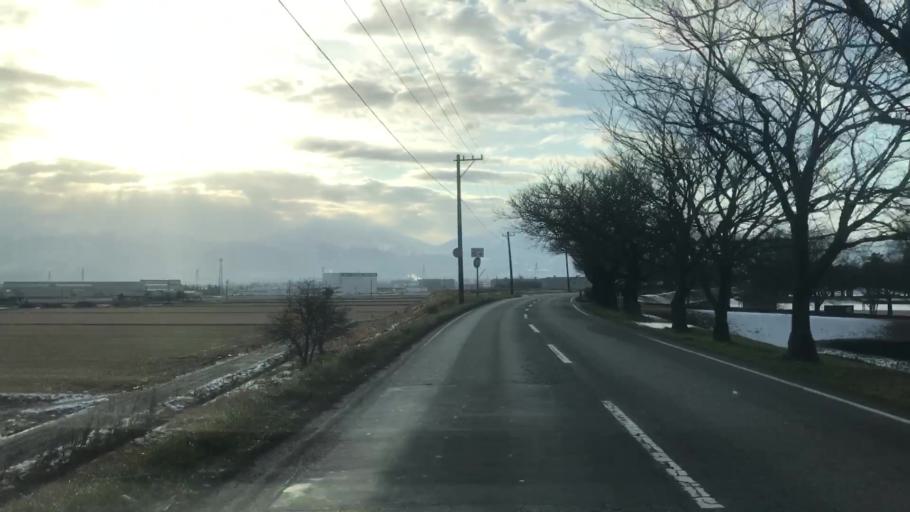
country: JP
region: Toyama
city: Toyama-shi
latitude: 36.7016
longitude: 137.2806
